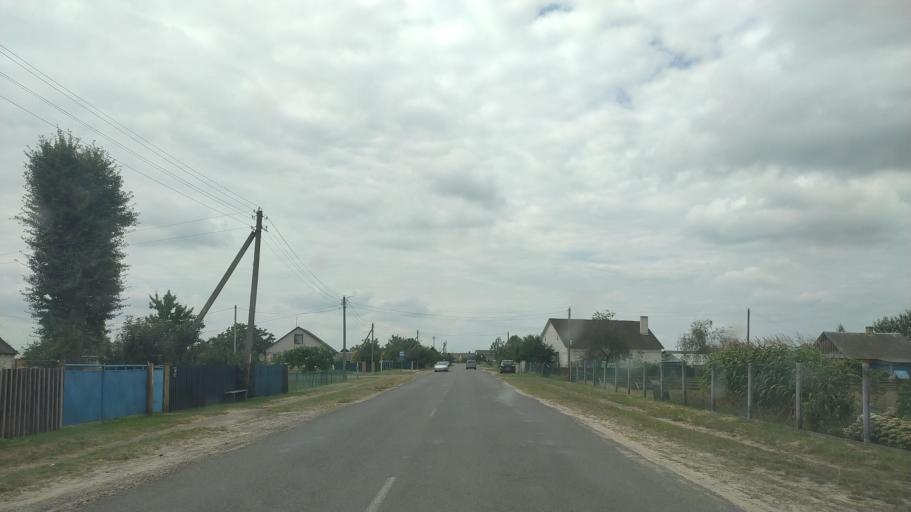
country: BY
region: Brest
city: Byaroza
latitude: 52.5414
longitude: 25.0857
